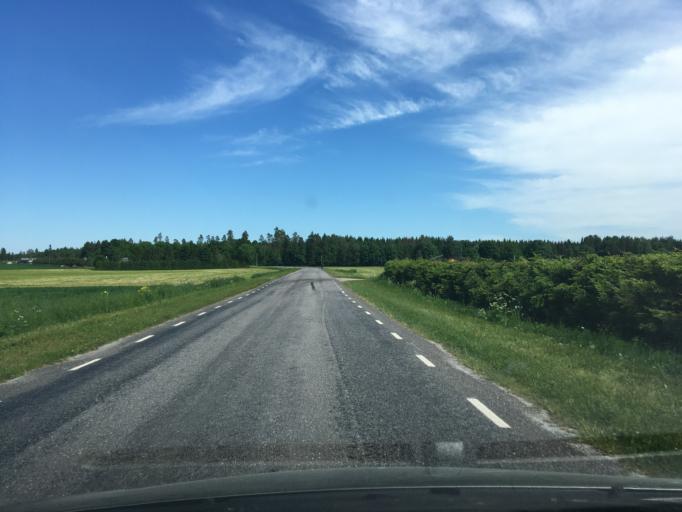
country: EE
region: Raplamaa
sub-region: Rapla vald
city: Rapla
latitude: 59.0569
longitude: 24.9061
